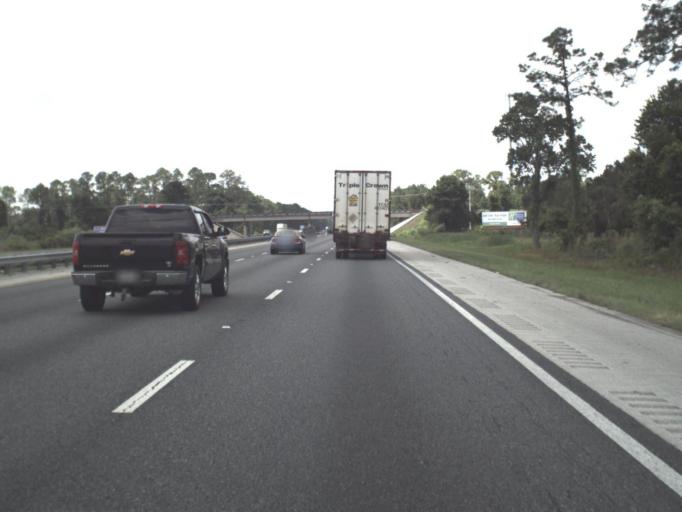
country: US
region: Florida
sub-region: Saint Johns County
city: Saint Augustine South
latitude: 29.8586
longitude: -81.3940
